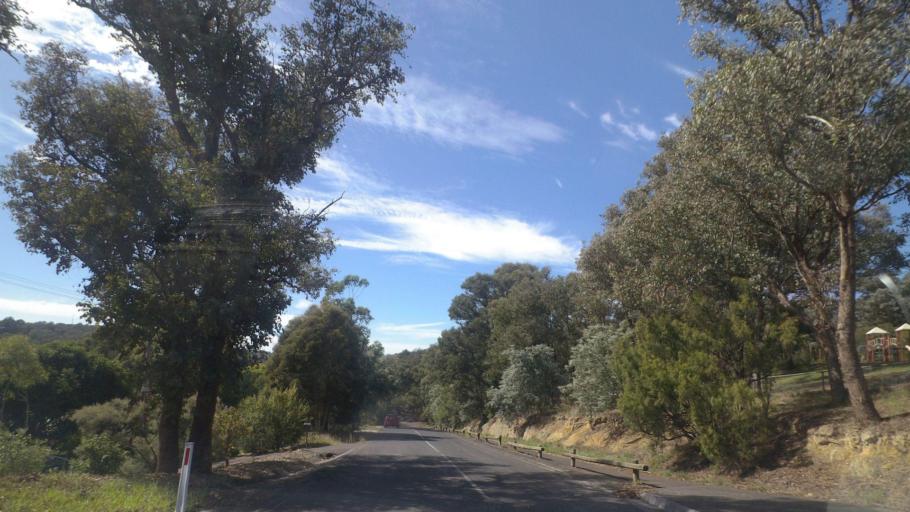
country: AU
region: Victoria
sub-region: Nillumbik
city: North Warrandyte
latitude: -37.7418
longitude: 145.2142
